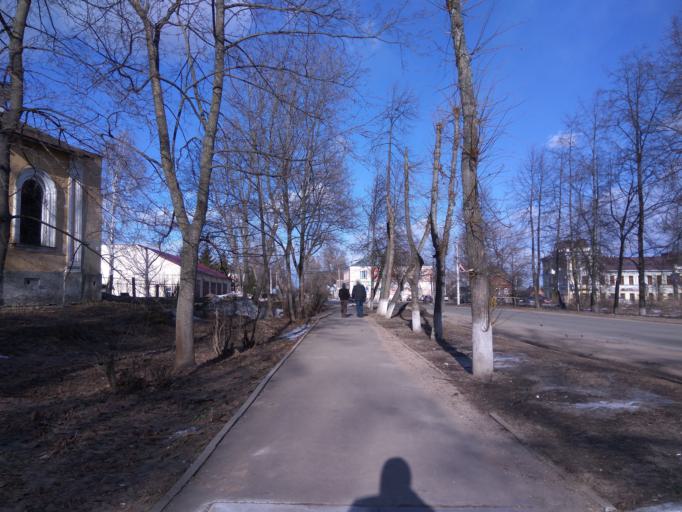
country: RU
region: Jaroslavl
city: Rostov
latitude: 57.1872
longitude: 39.4259
